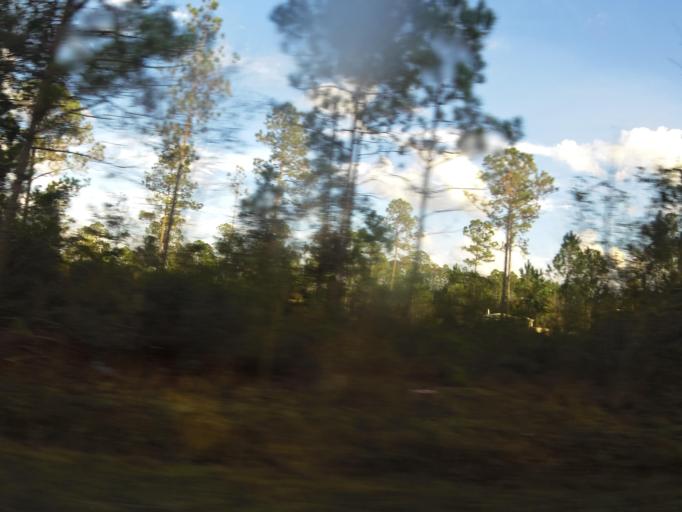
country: US
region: Florida
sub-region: Duval County
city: Baldwin
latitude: 30.1909
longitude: -81.9910
